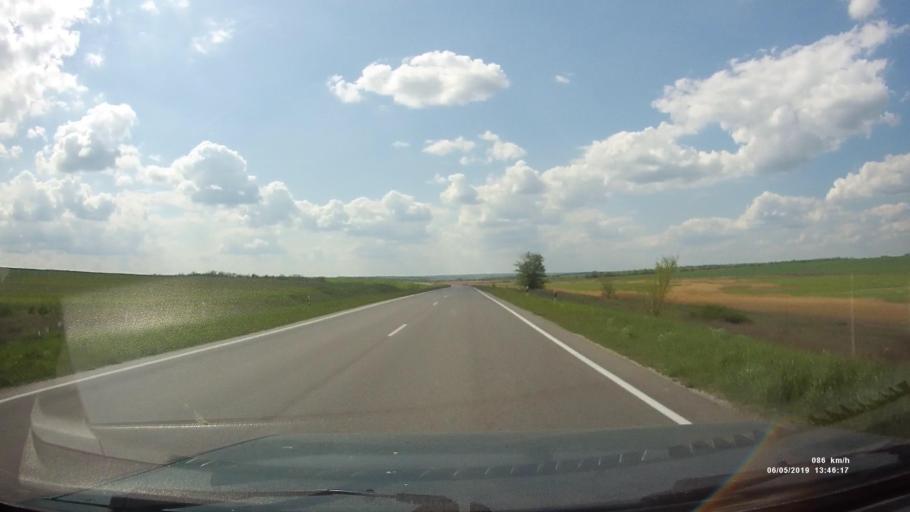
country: RU
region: Rostov
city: Melikhovskaya
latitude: 47.6576
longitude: 40.5845
